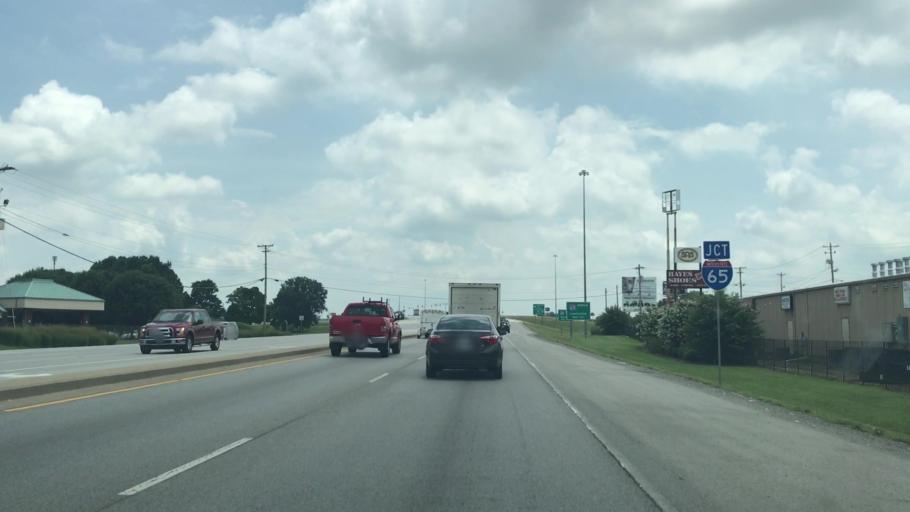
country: US
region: Kentucky
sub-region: Warren County
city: Bowling Green
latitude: 36.9391
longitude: -86.4204
